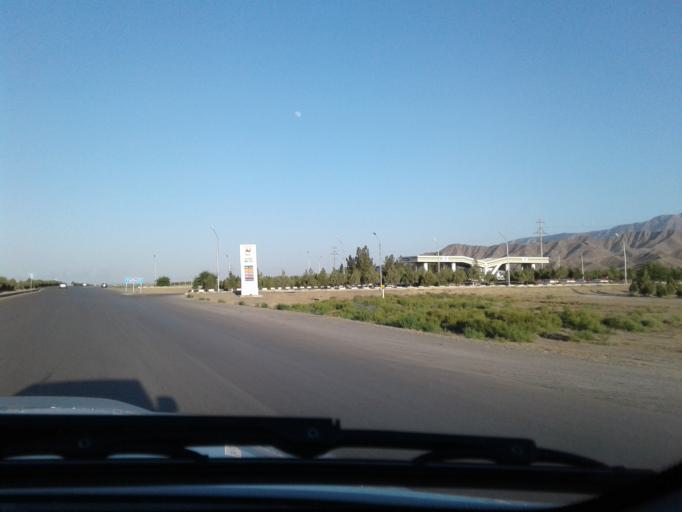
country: TM
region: Ahal
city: Baharly
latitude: 38.2760
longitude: 57.6853
